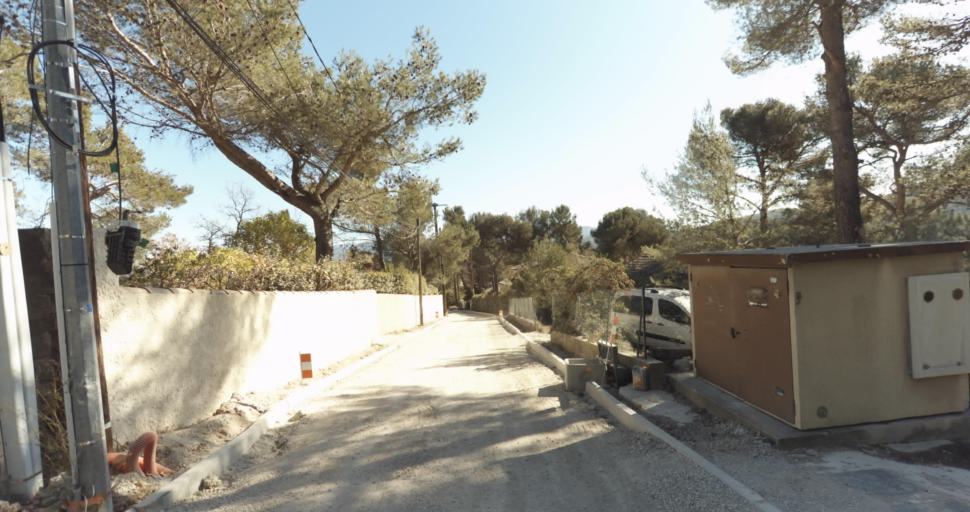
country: FR
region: Provence-Alpes-Cote d'Azur
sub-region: Departement des Bouches-du-Rhone
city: Peypin
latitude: 43.3868
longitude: 5.5725
